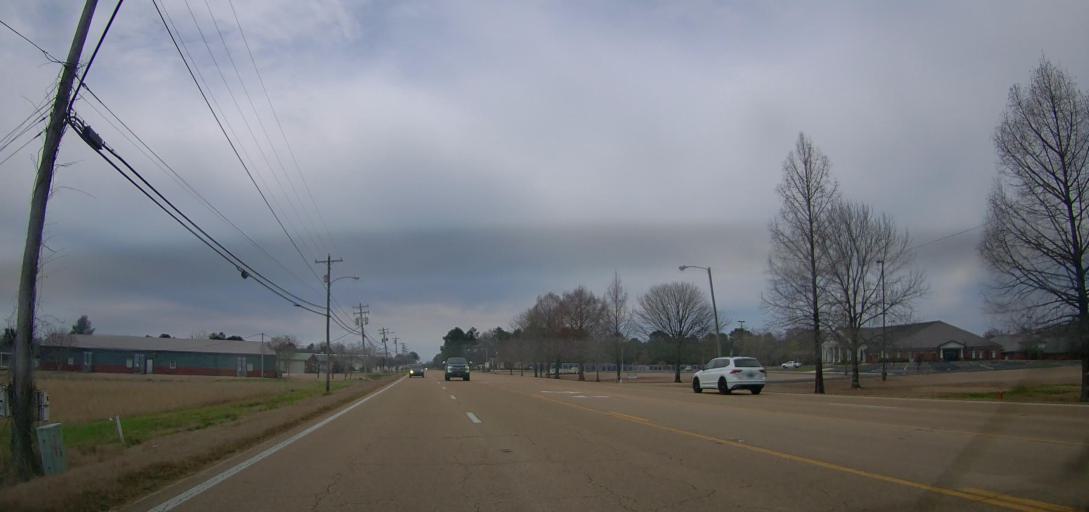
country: US
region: Mississippi
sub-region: Lee County
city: Tupelo
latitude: 34.2908
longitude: -88.7499
